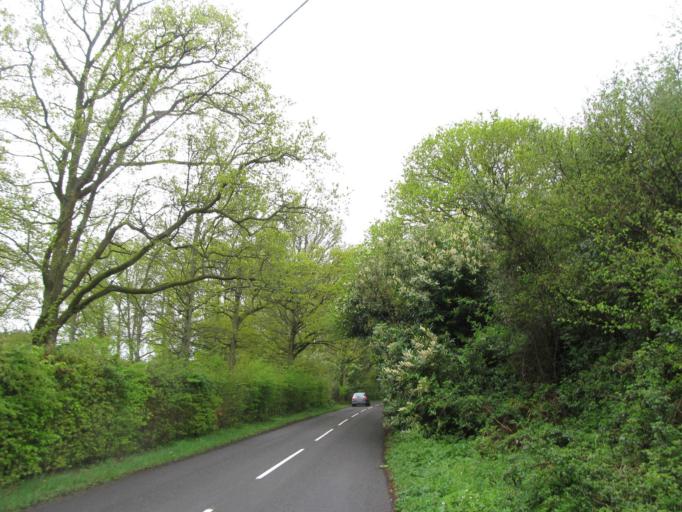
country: GB
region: England
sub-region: Surrey
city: Chiddingfold
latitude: 51.0792
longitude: -0.6357
